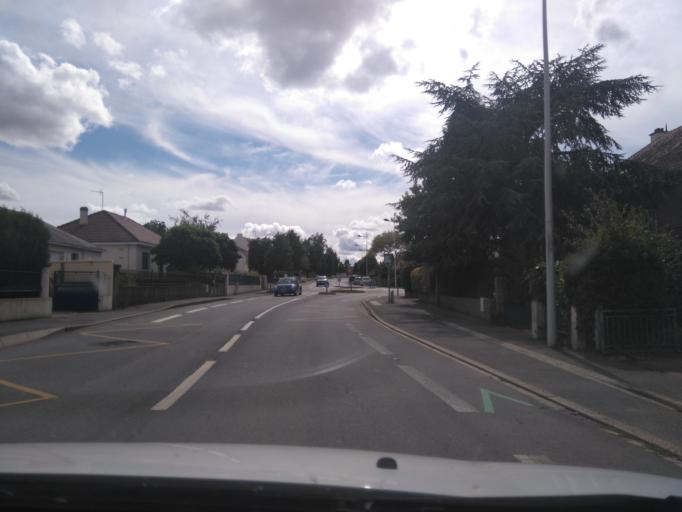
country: FR
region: Pays de la Loire
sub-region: Departement de la Loire-Atlantique
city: Reze
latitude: 47.1735
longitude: -1.5709
